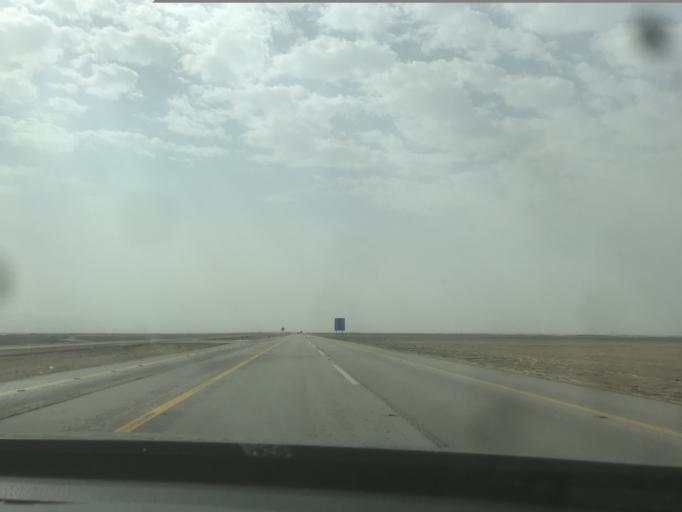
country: SA
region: Eastern Province
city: Dhahran
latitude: 26.0057
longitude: 49.9933
